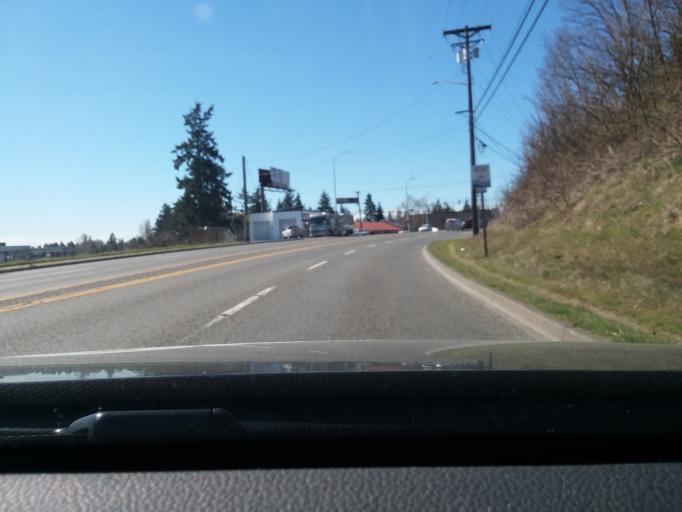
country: US
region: Washington
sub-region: Pierce County
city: Fircrest
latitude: 47.2316
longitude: -122.4818
